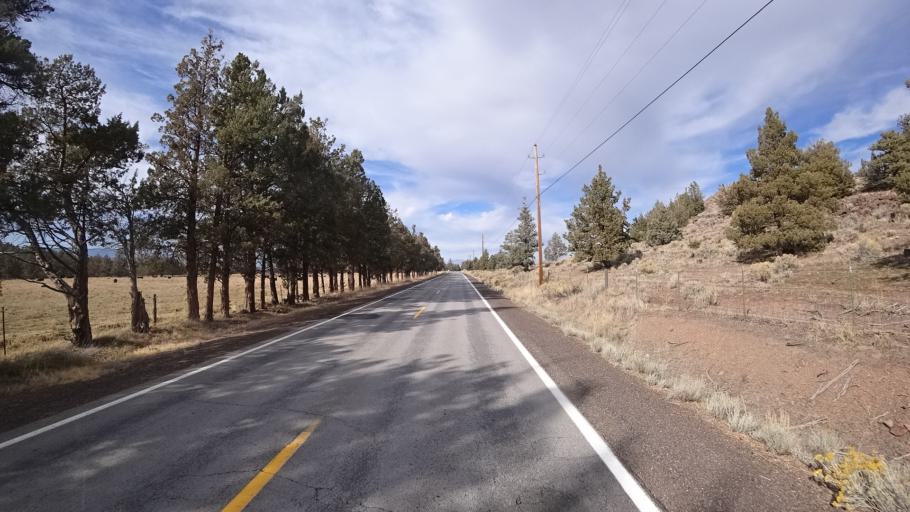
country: US
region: California
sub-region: Siskiyou County
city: Weed
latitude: 41.5783
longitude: -122.3969
